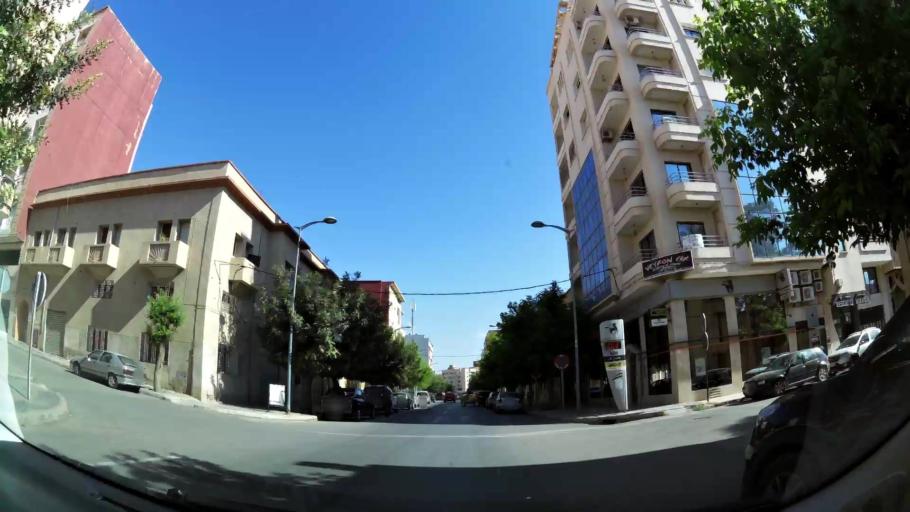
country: MA
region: Oriental
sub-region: Oujda-Angad
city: Oujda
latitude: 34.6888
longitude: -1.9173
